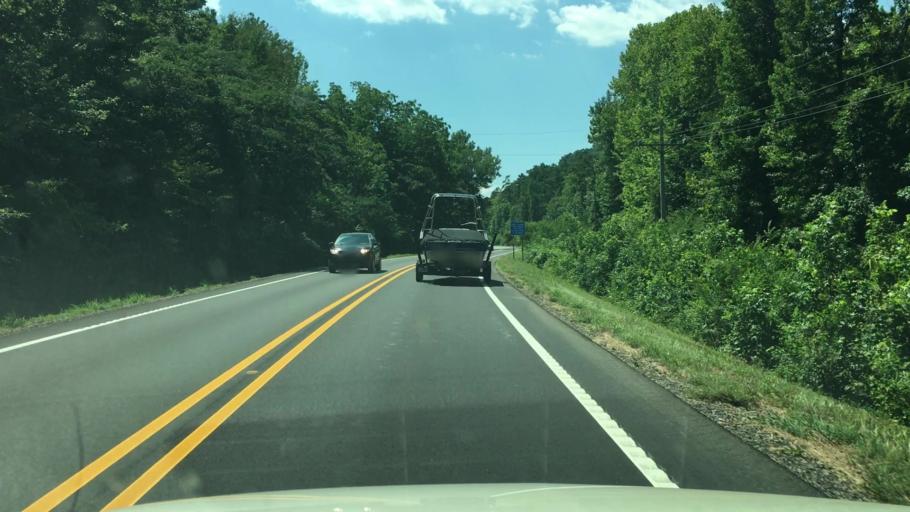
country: US
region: Arkansas
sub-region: Garland County
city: Rockwell
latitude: 34.5168
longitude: -93.2995
